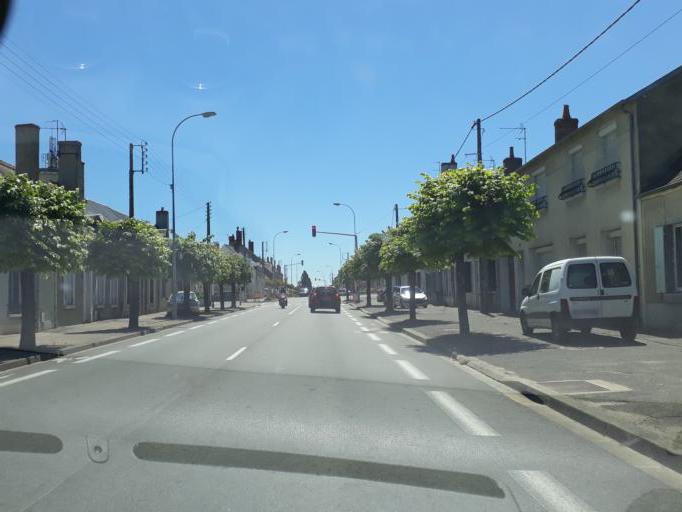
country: FR
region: Centre
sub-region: Departement du Cher
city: Mehun-sur-Yevre
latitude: 47.1485
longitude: 2.2168
